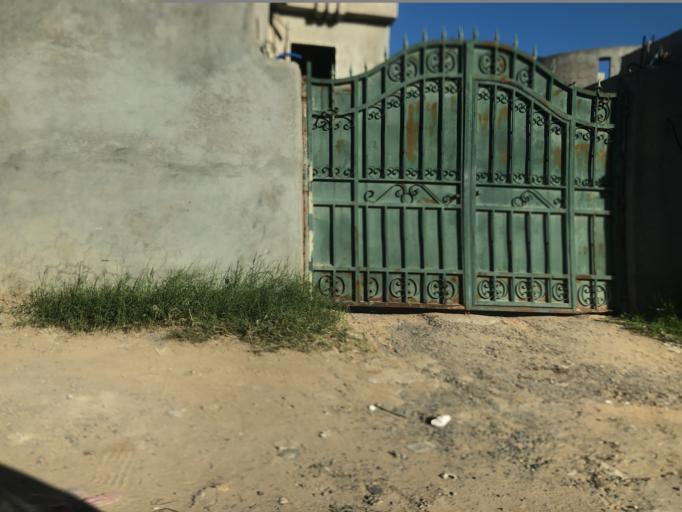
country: LY
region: Tripoli
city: Tagiura
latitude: 32.8673
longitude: 13.2889
